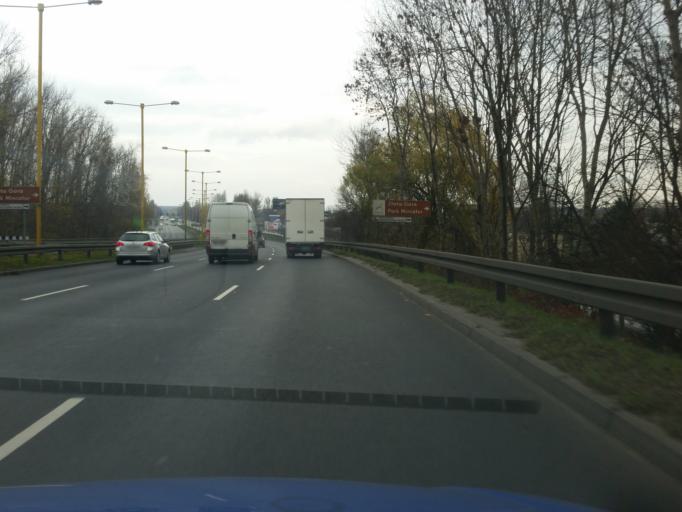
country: PL
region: Silesian Voivodeship
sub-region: Czestochowa
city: Czestochowa
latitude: 50.8015
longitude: 19.1339
